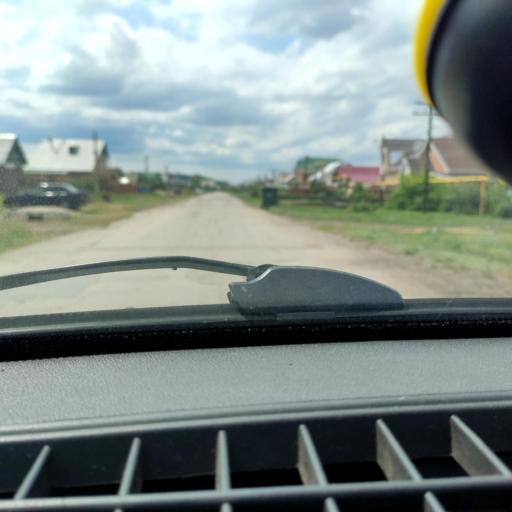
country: RU
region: Samara
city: Povolzhskiy
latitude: 53.6386
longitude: 49.6794
